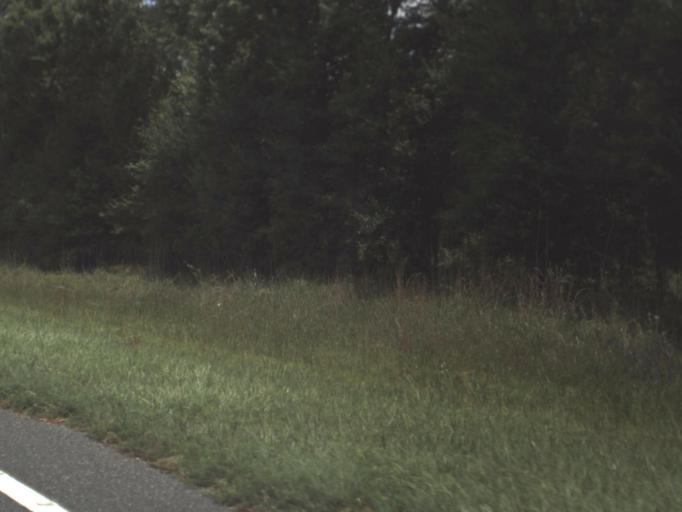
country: US
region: Florida
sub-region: Taylor County
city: Perry
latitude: 29.9558
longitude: -83.4628
